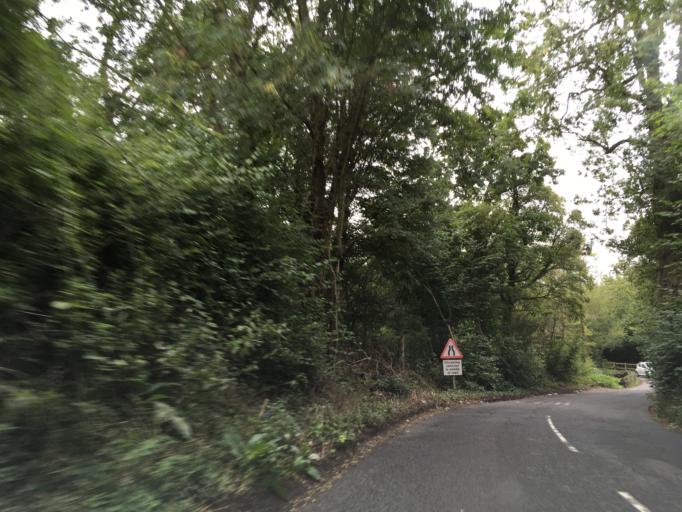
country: GB
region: England
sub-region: South Gloucestershire
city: Siston
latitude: 51.4731
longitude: -2.4521
